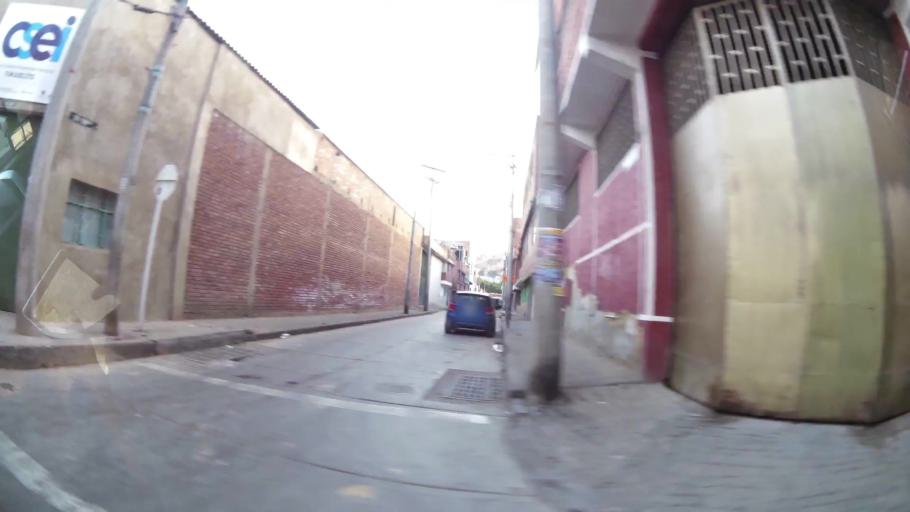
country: CO
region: Bogota D.C.
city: Bogota
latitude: 4.5633
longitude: -74.1354
